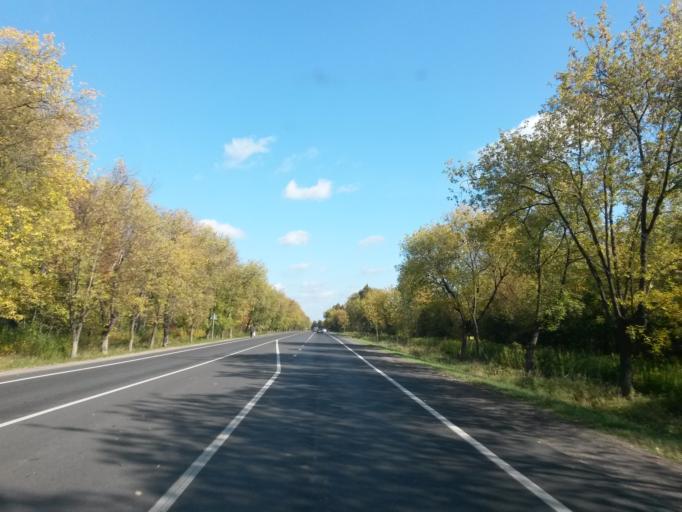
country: RU
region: Moskovskaya
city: L'vovskiy
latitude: 55.2950
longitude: 37.5216
